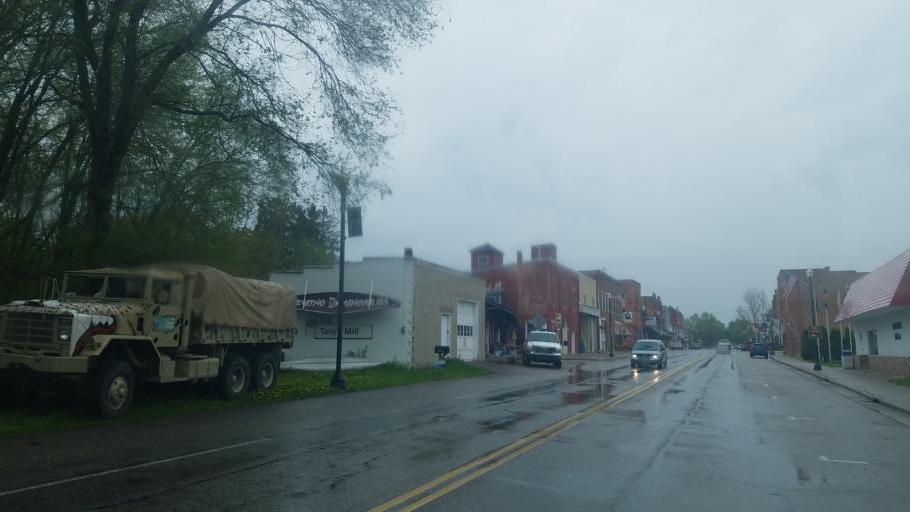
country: US
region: Wisconsin
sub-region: Juneau County
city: Elroy
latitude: 43.6519
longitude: -90.2230
